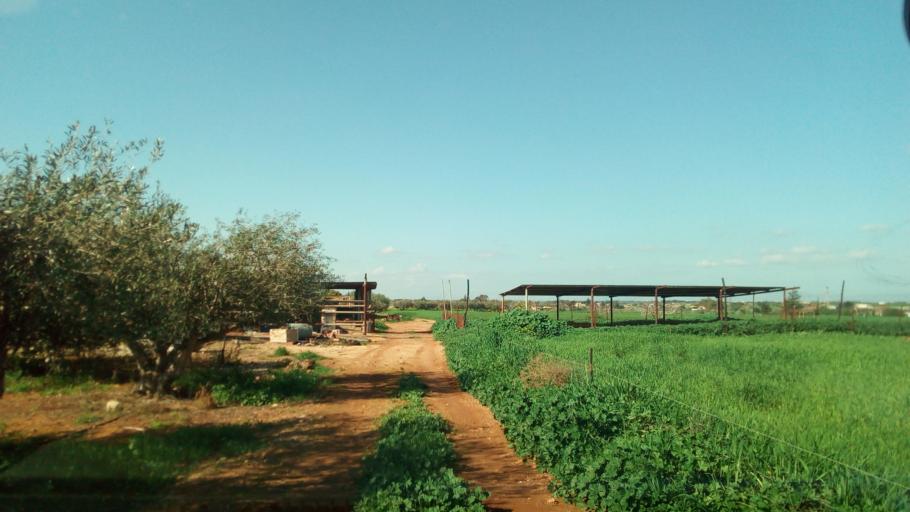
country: CY
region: Ammochostos
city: Avgorou
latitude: 35.0384
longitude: 33.8548
